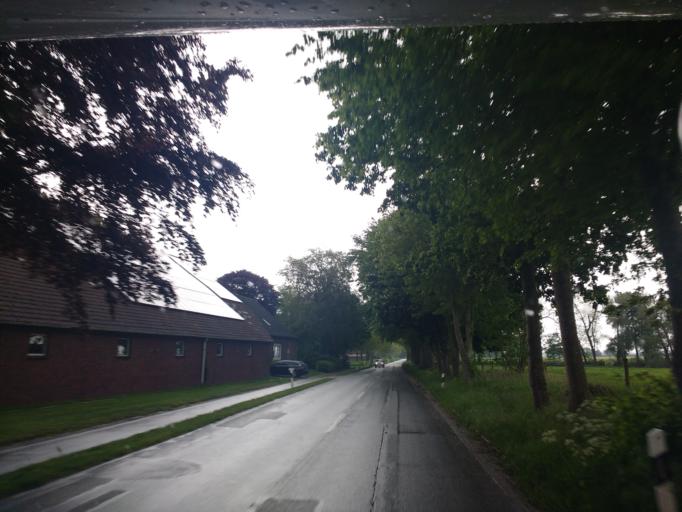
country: DE
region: Lower Saxony
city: Schillig
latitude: 53.7031
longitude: 7.9912
